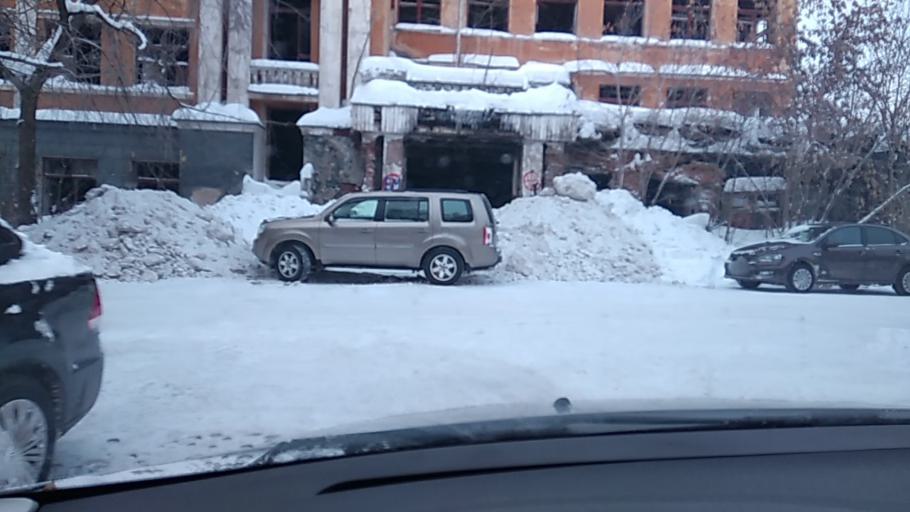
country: RU
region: Sverdlovsk
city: Yekaterinburg
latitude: 56.8200
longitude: 60.6013
